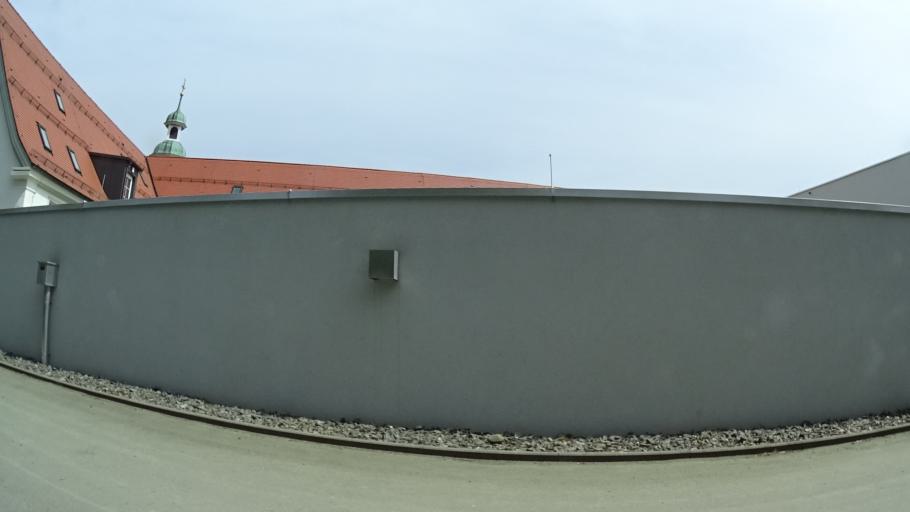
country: DE
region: Baden-Wuerttemberg
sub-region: Freiburg Region
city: Rottweil
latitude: 48.1507
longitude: 8.6341
